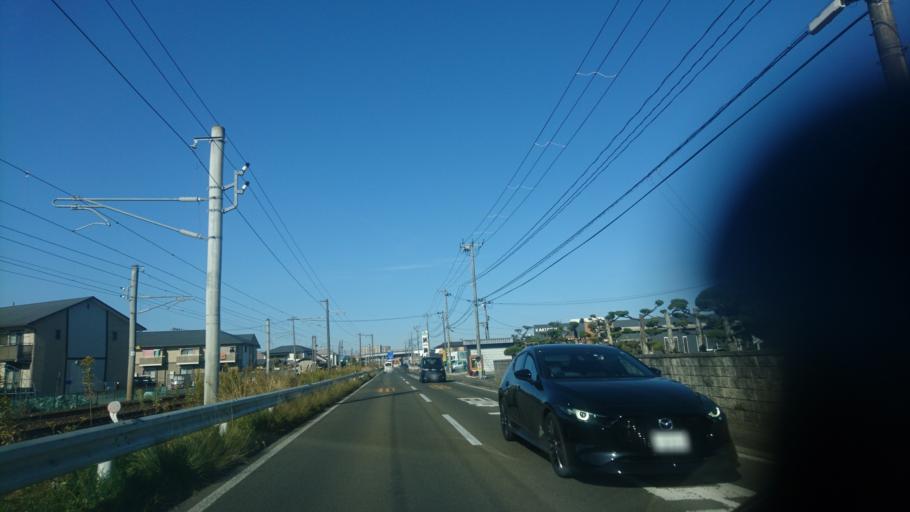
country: JP
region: Miyagi
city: Iwanuma
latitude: 38.1616
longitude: 140.8855
